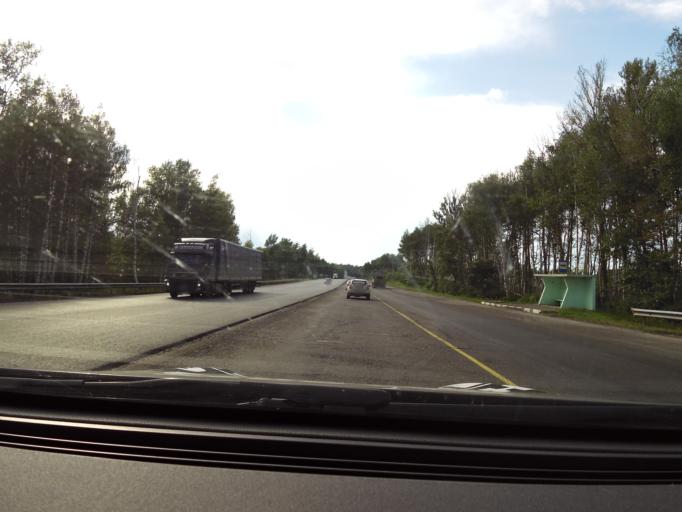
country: RU
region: Vladimir
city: Novovyazniki
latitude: 56.1977
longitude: 42.3669
